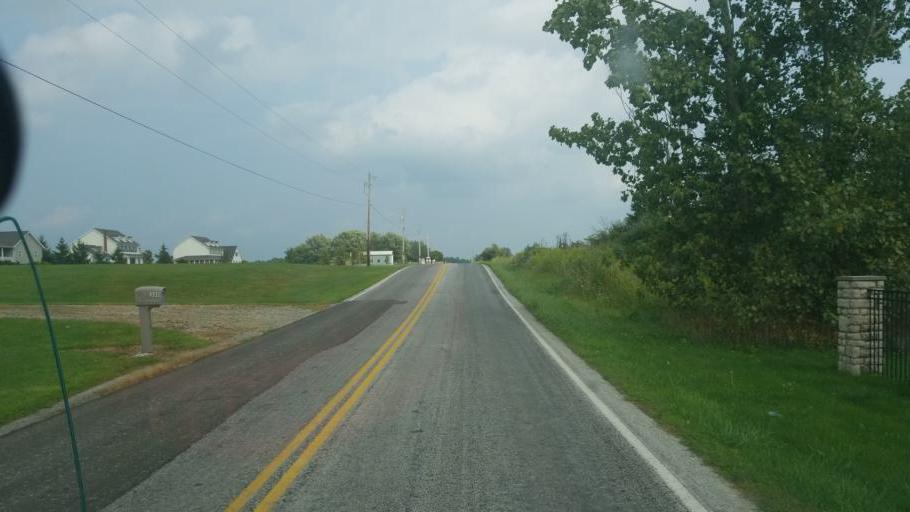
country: US
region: Ohio
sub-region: Lorain County
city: Wellington
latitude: 41.0582
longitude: -82.1863
